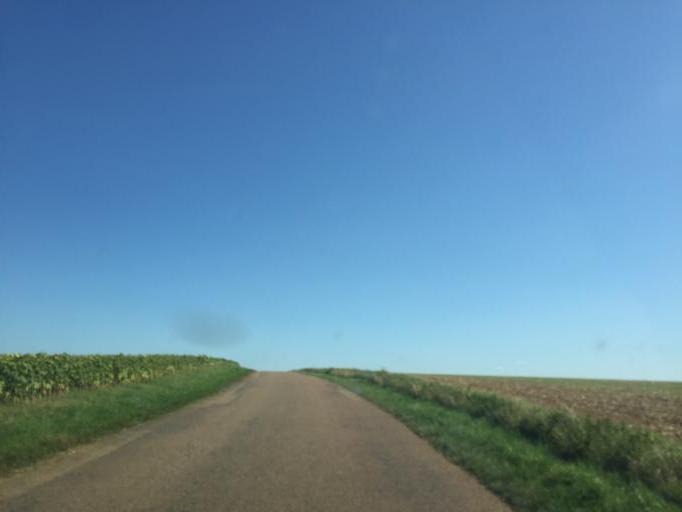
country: FR
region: Bourgogne
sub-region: Departement de l'Yonne
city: Fontenailles
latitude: 47.5340
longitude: 3.3422
